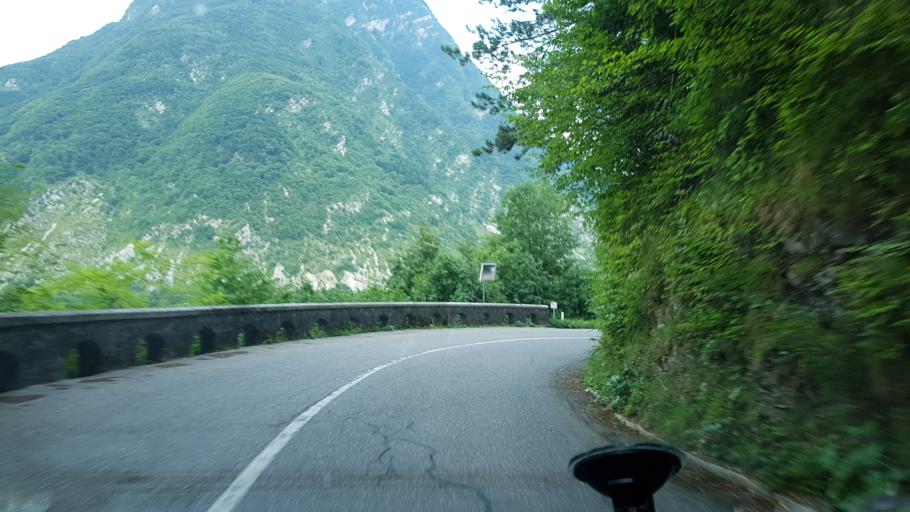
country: SI
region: Bovec
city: Bovec
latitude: 46.3044
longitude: 13.4780
